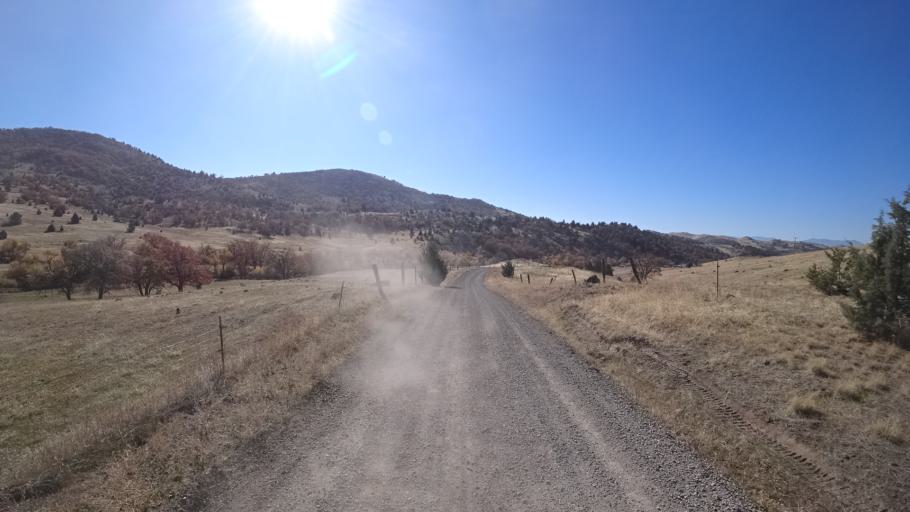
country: US
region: California
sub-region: Siskiyou County
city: Montague
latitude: 41.7958
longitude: -122.3366
